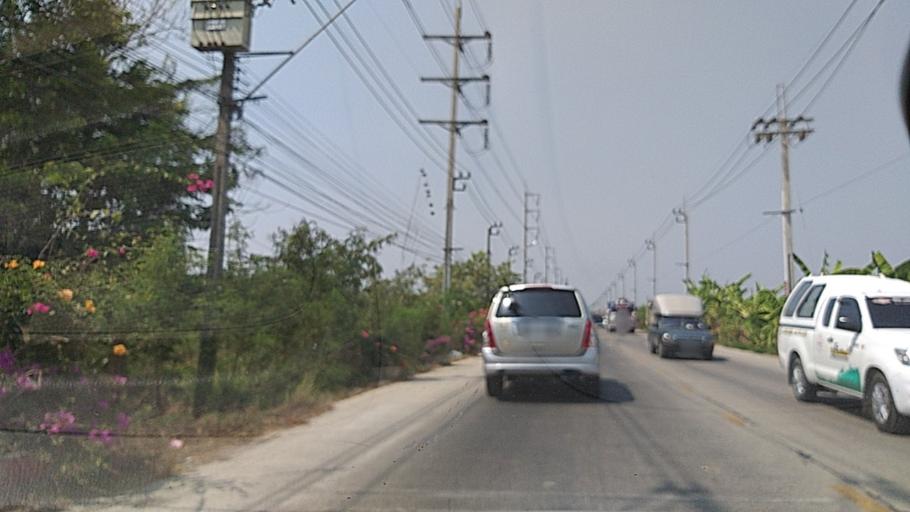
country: TH
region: Nonthaburi
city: Sai Noi
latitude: 13.9684
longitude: 100.3104
